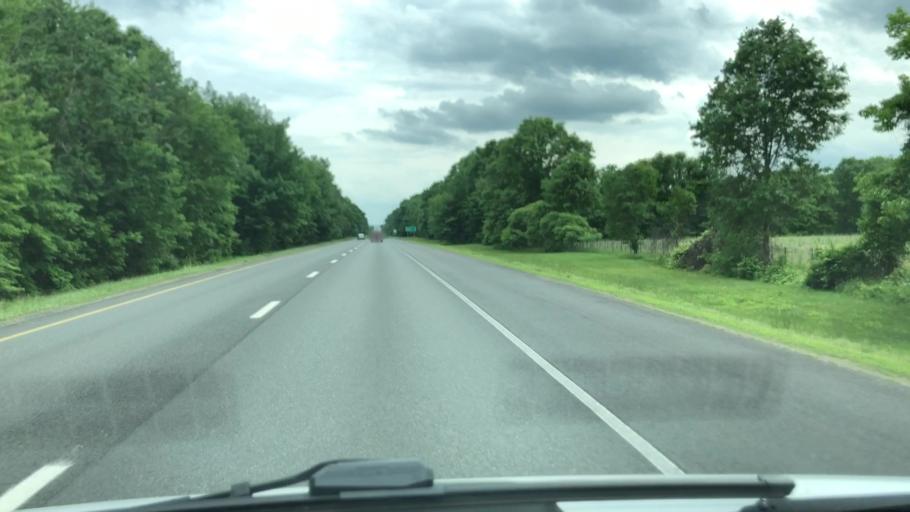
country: US
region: Massachusetts
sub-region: Franklin County
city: Whately
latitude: 42.4279
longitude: -72.6232
